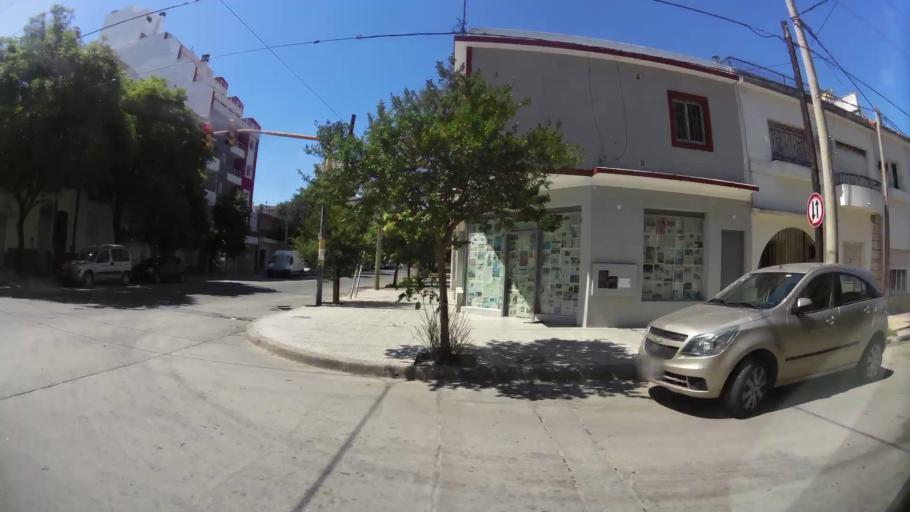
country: AR
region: Cordoba
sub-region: Departamento de Capital
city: Cordoba
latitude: -31.3990
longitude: -64.1913
